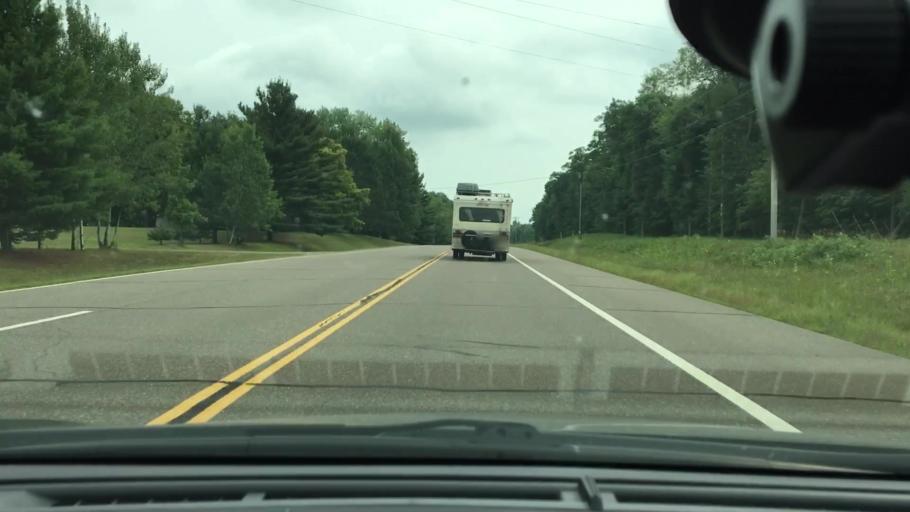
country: US
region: Minnesota
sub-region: Crow Wing County
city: Crosby
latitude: 46.4103
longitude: -93.8458
